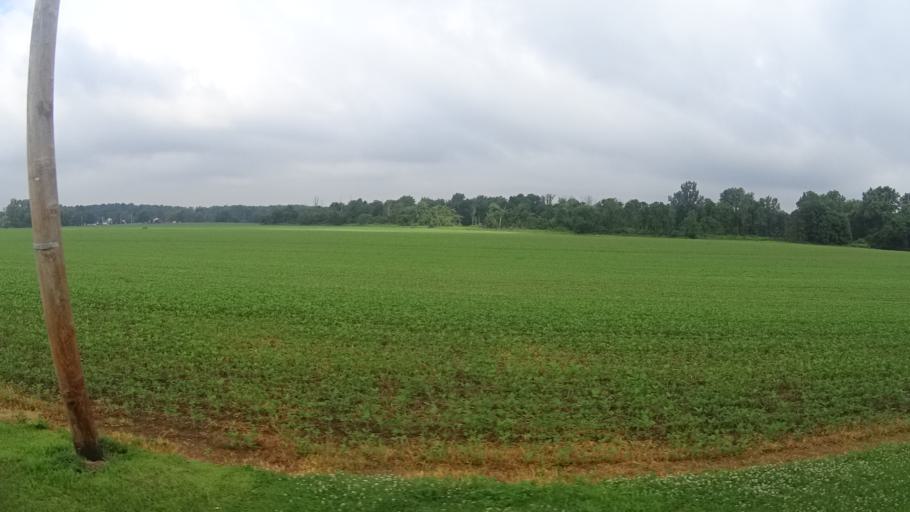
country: US
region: Ohio
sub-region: Erie County
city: Huron
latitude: 41.3180
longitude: -82.4995
